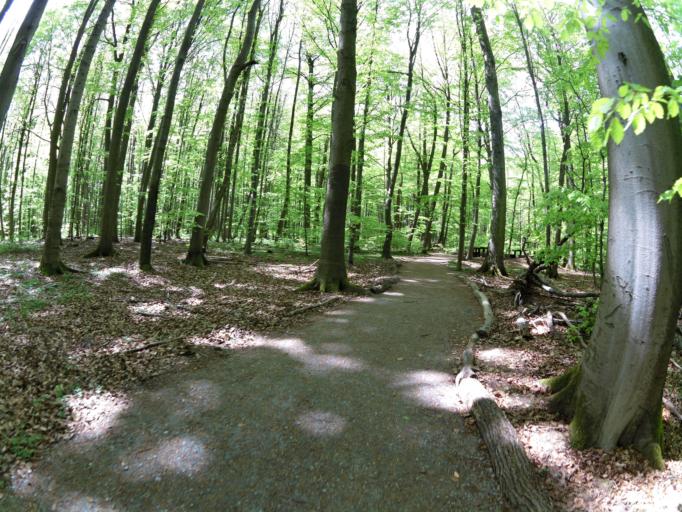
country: DE
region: Thuringia
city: Weberstedt
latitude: 51.0819
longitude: 10.5084
